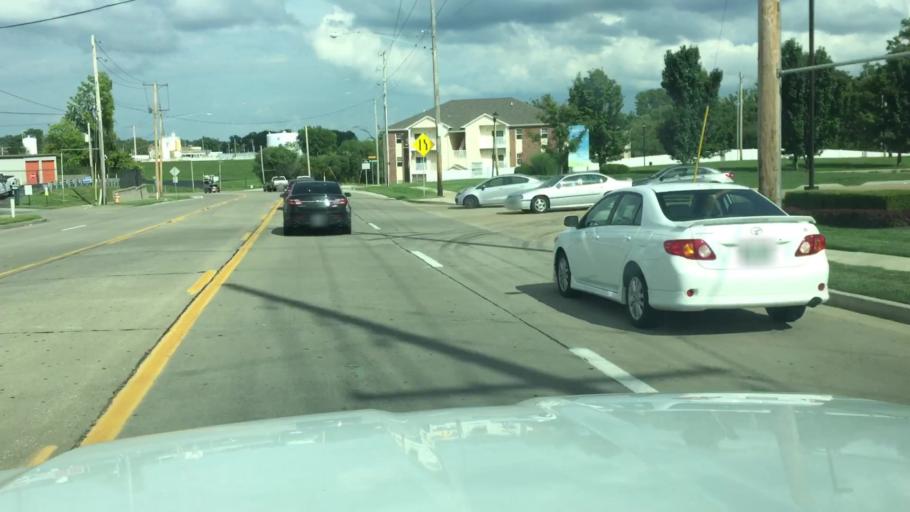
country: US
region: Missouri
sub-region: Jefferson County
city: Arnold
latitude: 38.4615
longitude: -90.3718
